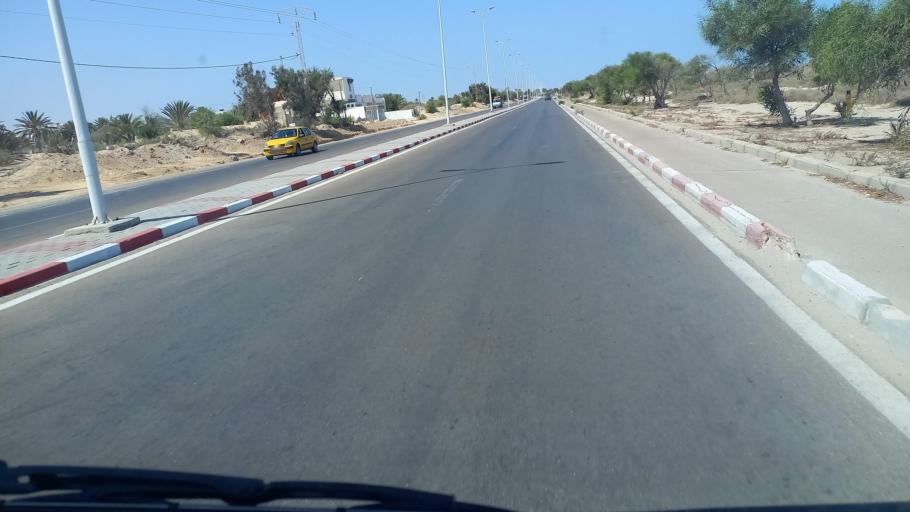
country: TN
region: Madanin
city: Midoun
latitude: 33.8692
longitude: 10.9516
